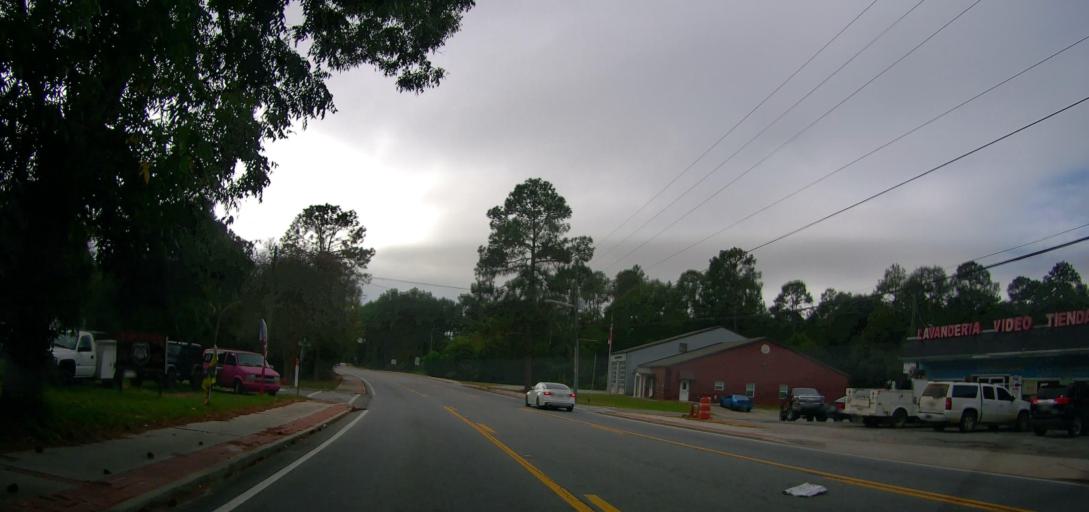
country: US
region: Georgia
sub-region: Tift County
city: Omega
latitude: 31.3389
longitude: -83.5973
